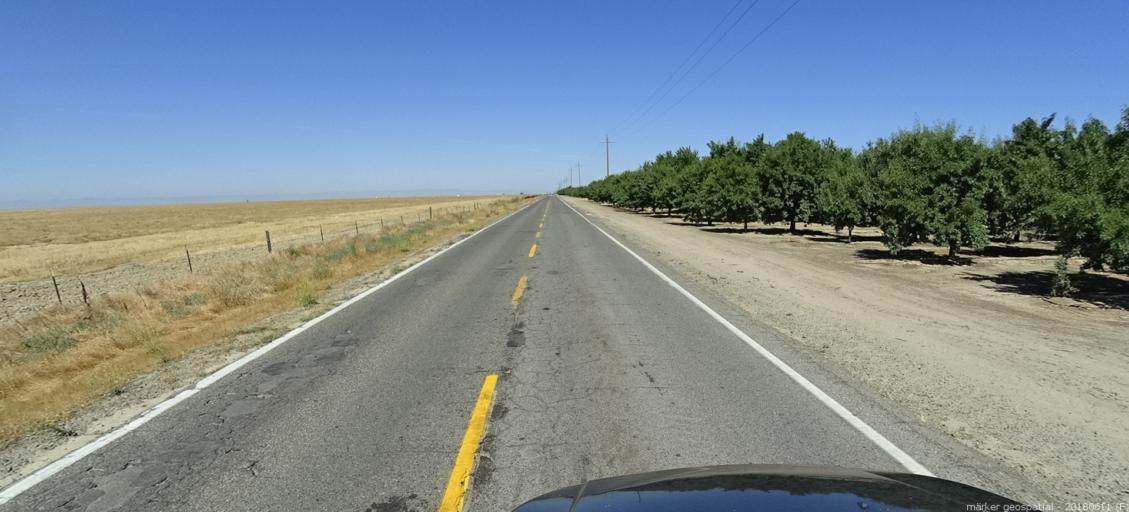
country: US
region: California
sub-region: Madera County
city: Madera
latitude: 36.9237
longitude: -120.1917
